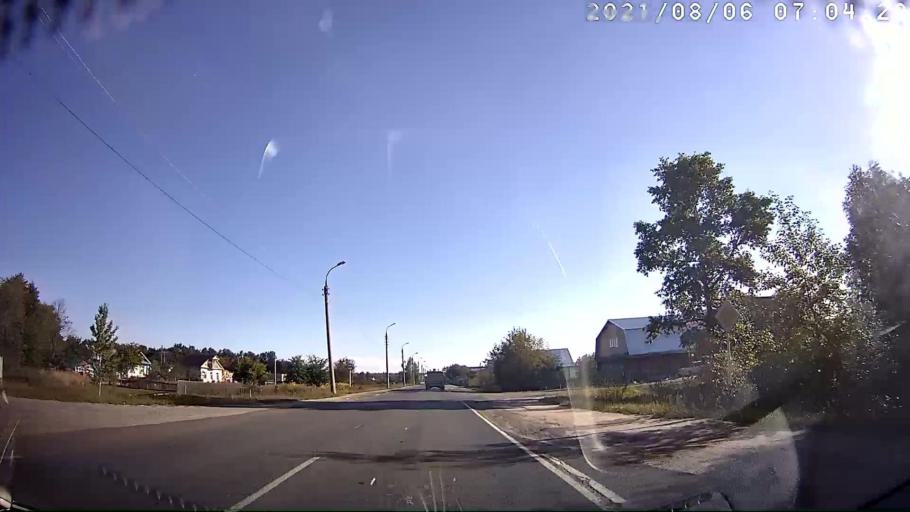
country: RU
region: Mariy-El
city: Yoshkar-Ola
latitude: 56.5462
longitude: 47.9818
